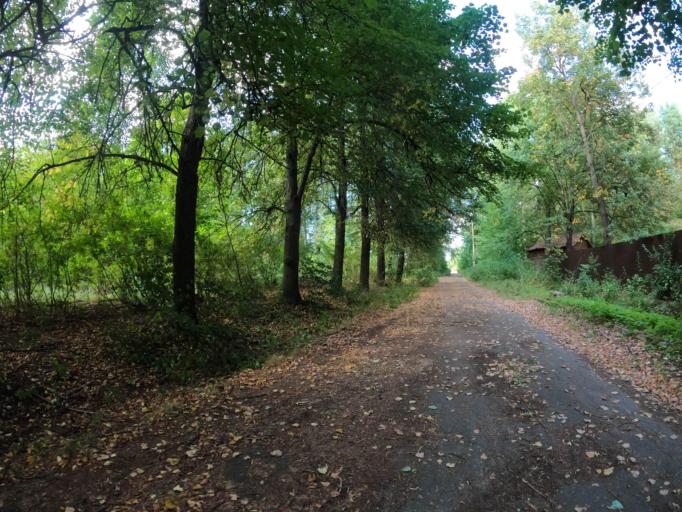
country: RU
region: Moskovskaya
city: Konobeyevo
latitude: 55.3907
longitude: 38.7103
